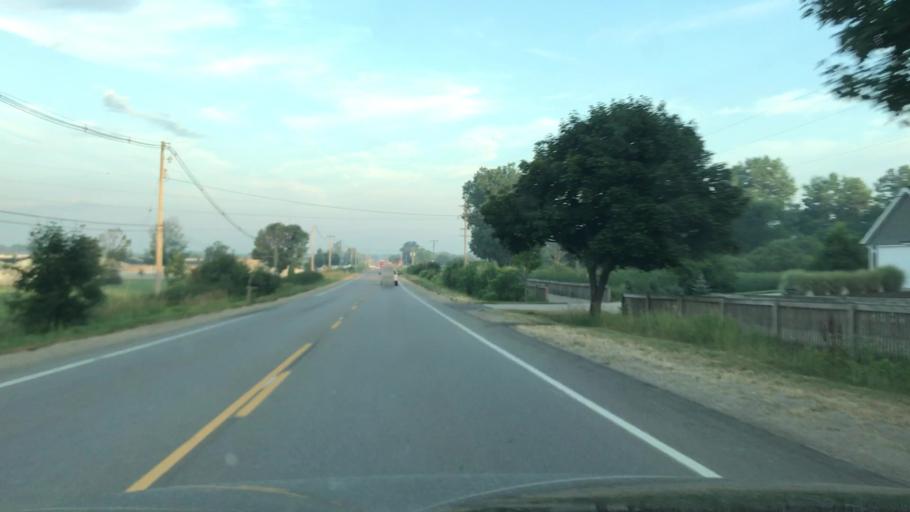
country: US
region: Michigan
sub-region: Ottawa County
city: Zeeland
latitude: 42.7834
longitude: -86.0103
